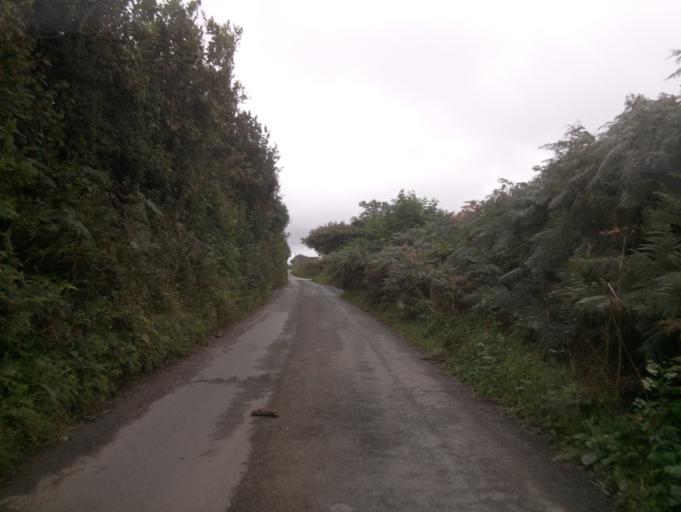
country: GB
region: England
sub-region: Devon
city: Kingsbridge
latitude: 50.3111
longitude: -3.7159
